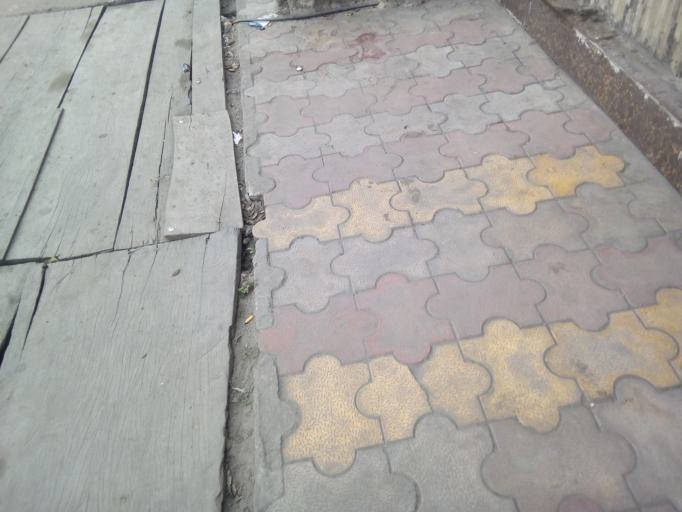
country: CD
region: Kinshasa
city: Kinshasa
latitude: -4.3199
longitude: 15.3036
